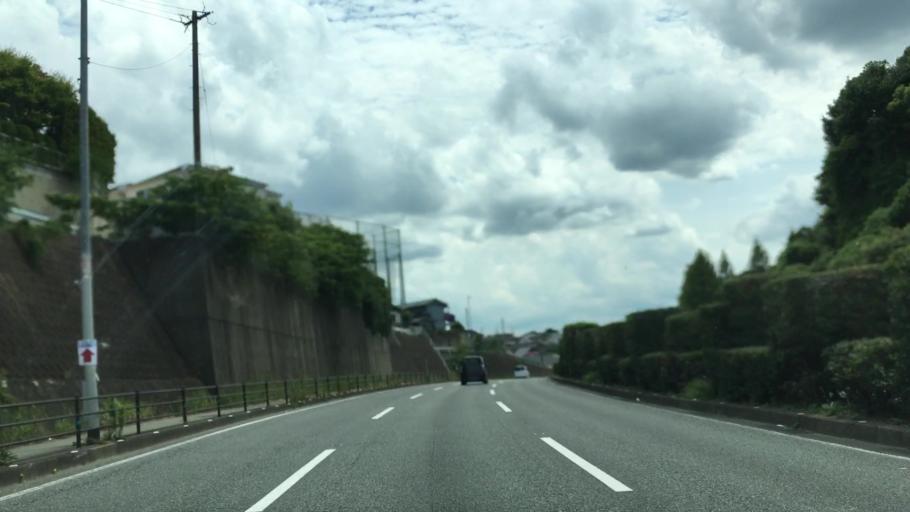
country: JP
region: Fukuoka
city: Dazaifu
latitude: 33.5055
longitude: 130.5296
